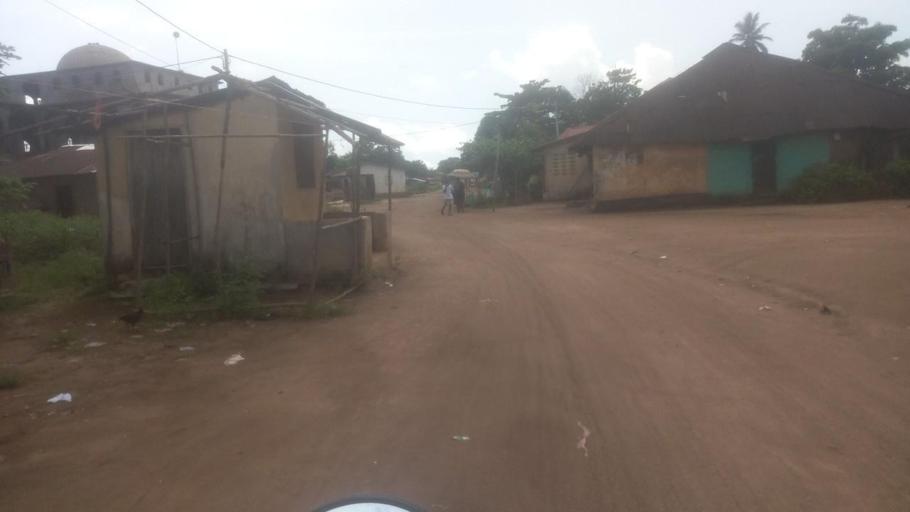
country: SL
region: Northern Province
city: Tintafor
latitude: 8.6301
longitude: -13.2163
